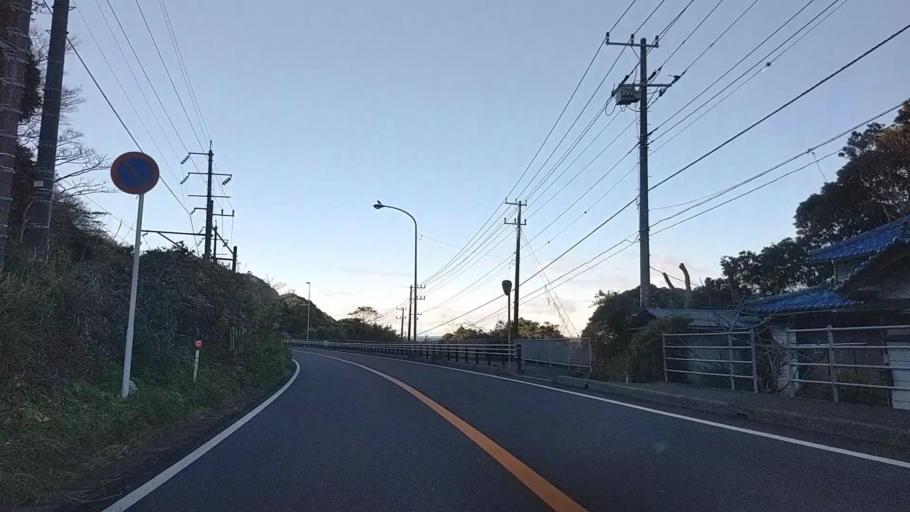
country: JP
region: Chiba
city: Futtsu
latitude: 35.2126
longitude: 139.8493
